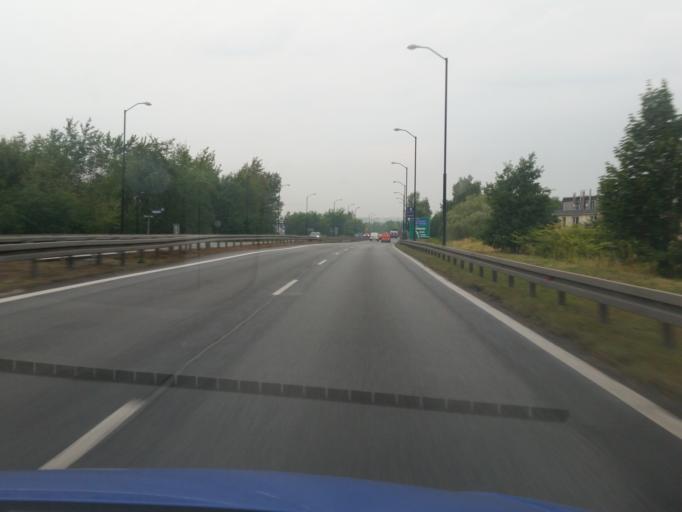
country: PL
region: Silesian Voivodeship
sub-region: Sosnowiec
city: Sosnowiec
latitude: 50.2561
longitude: 19.0828
